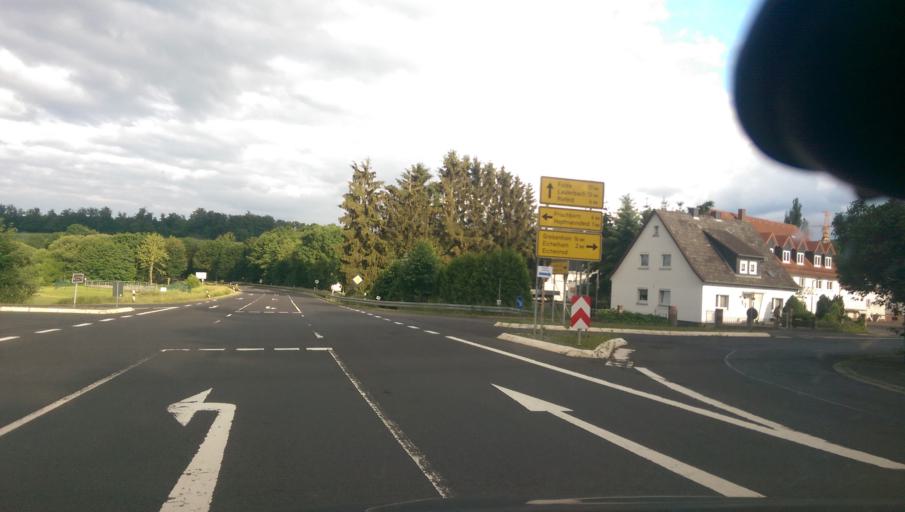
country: DE
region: Hesse
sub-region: Regierungsbezirk Giessen
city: Lautertal
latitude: 50.5813
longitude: 9.2996
